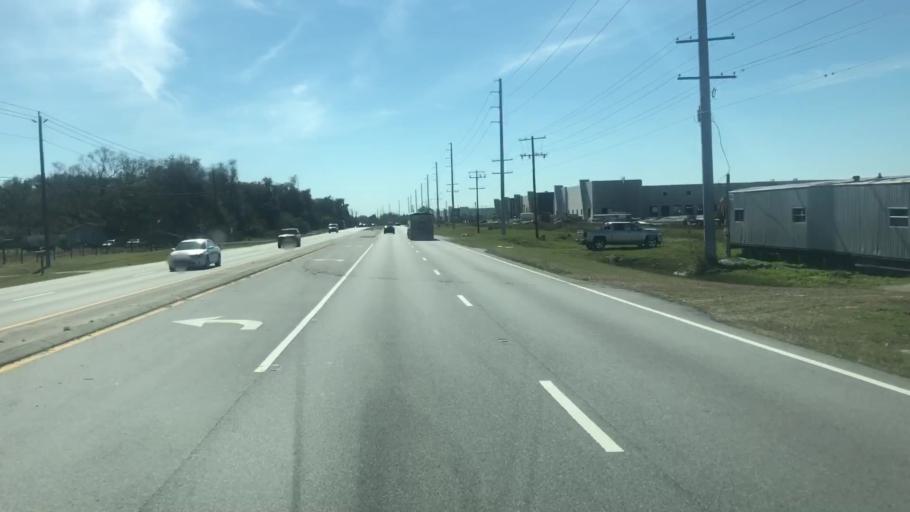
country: US
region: Florida
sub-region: Polk County
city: Winston
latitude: 28.0015
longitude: -82.0559
